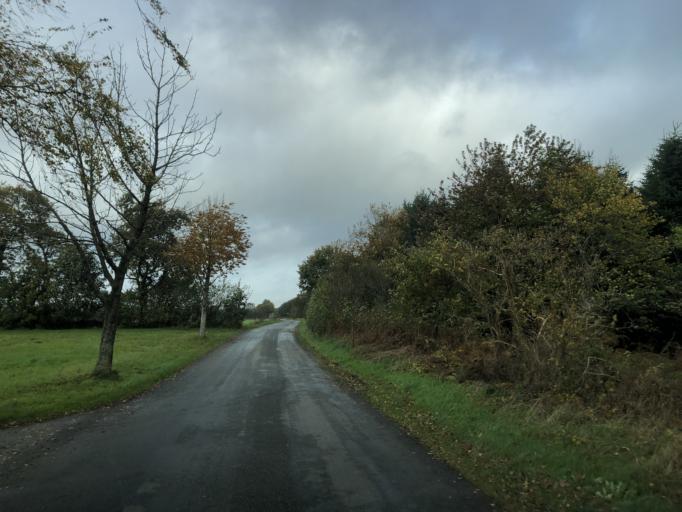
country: DK
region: South Denmark
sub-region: Vejen Kommune
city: Vejen
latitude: 55.4499
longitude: 9.1102
